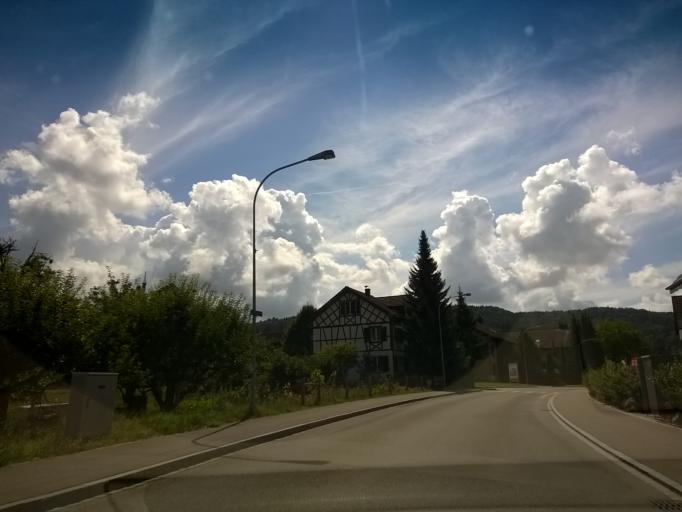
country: CH
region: Zurich
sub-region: Bezirk Buelach
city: Embrach / Embrach (Dorfkern)
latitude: 47.4873
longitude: 8.6187
